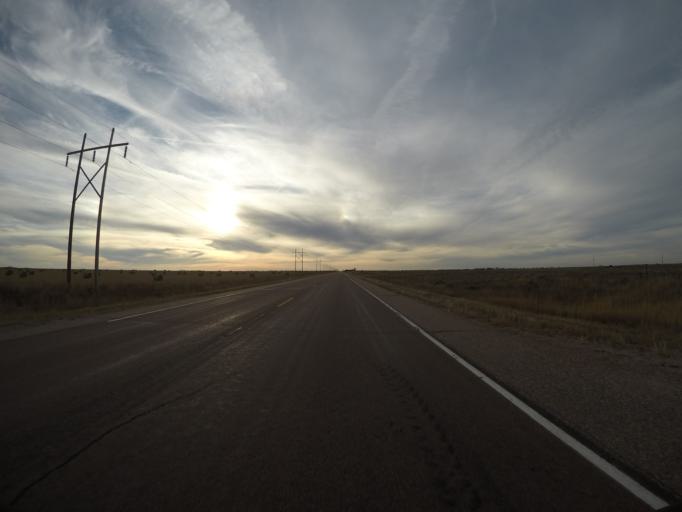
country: US
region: Colorado
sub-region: Yuma County
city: Yuma
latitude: 39.6558
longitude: -102.7261
